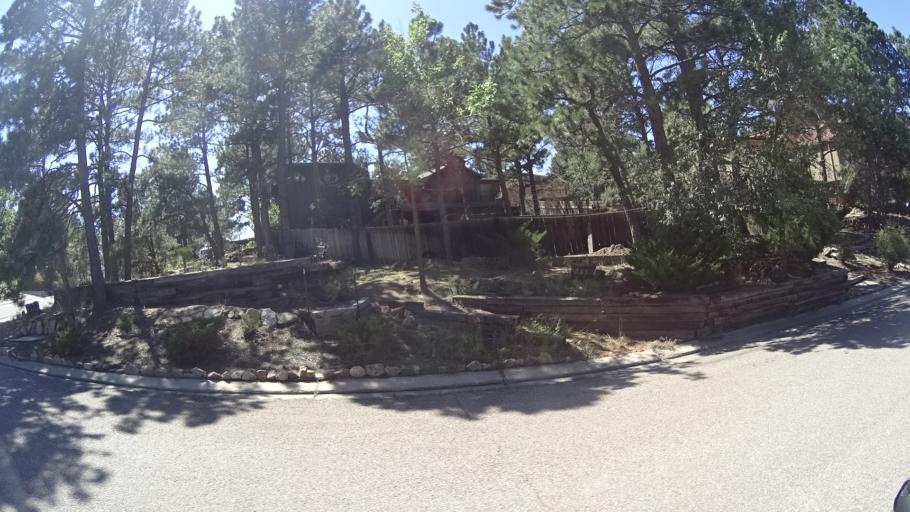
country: US
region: Colorado
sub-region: El Paso County
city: Colorado Springs
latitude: 38.9204
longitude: -104.7979
